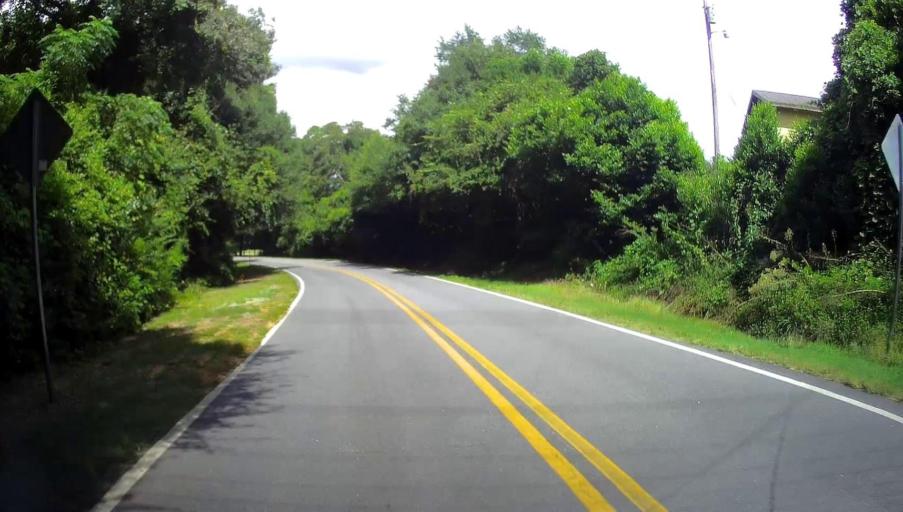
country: US
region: Georgia
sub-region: Chattahoochee County
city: Cusseta
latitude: 32.3049
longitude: -84.7711
